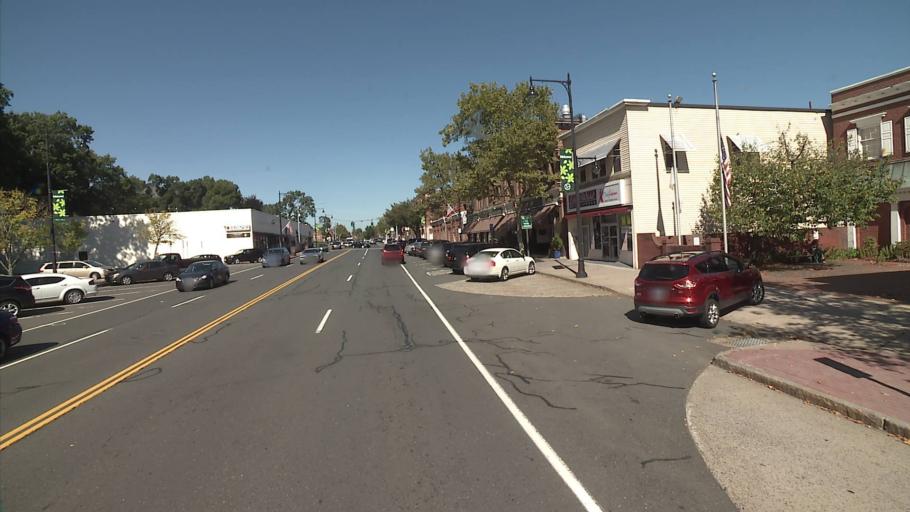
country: US
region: Connecticut
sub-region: Hartford County
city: Manchester
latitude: 41.7683
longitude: -72.5206
